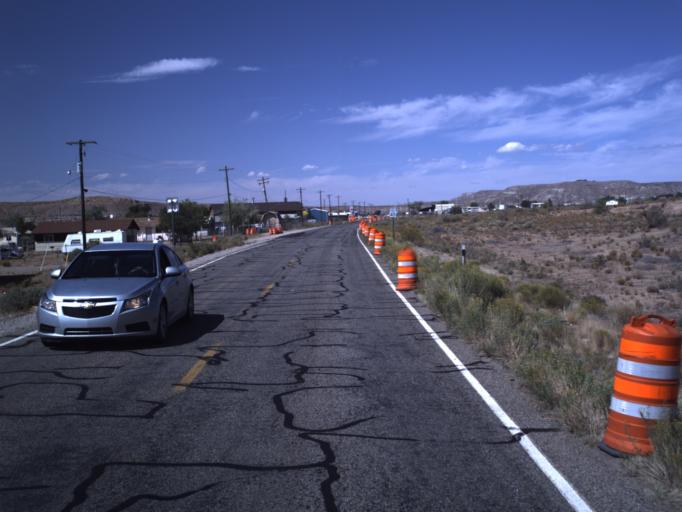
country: US
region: Utah
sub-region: San Juan County
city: Blanding
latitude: 37.2584
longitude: -109.2957
